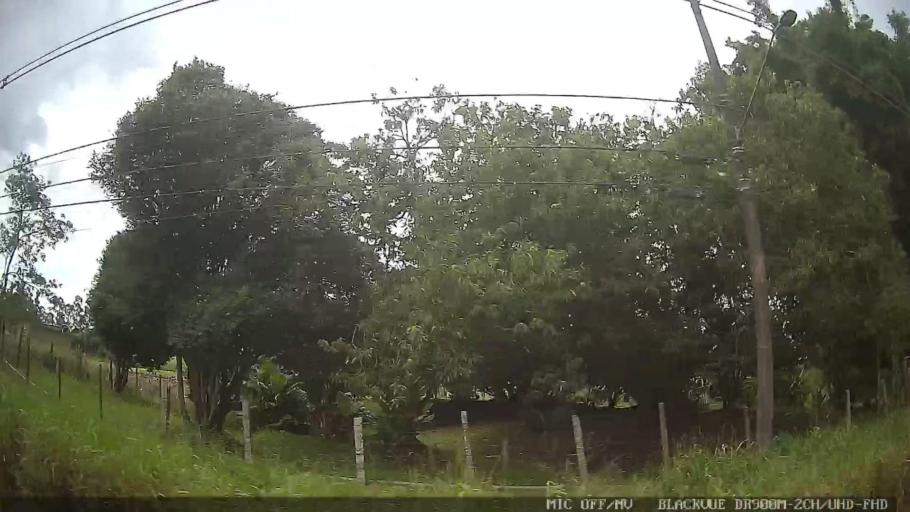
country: BR
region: Sao Paulo
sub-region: Suzano
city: Suzano
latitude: -23.6305
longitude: -46.2805
